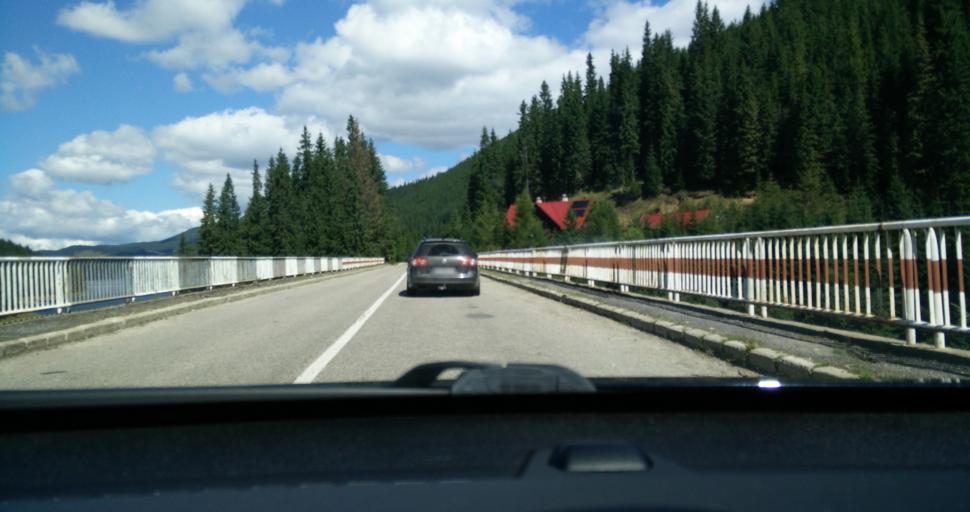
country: RO
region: Alba
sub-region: Comuna Sugag
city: Sugag
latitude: 45.5400
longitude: 23.6388
